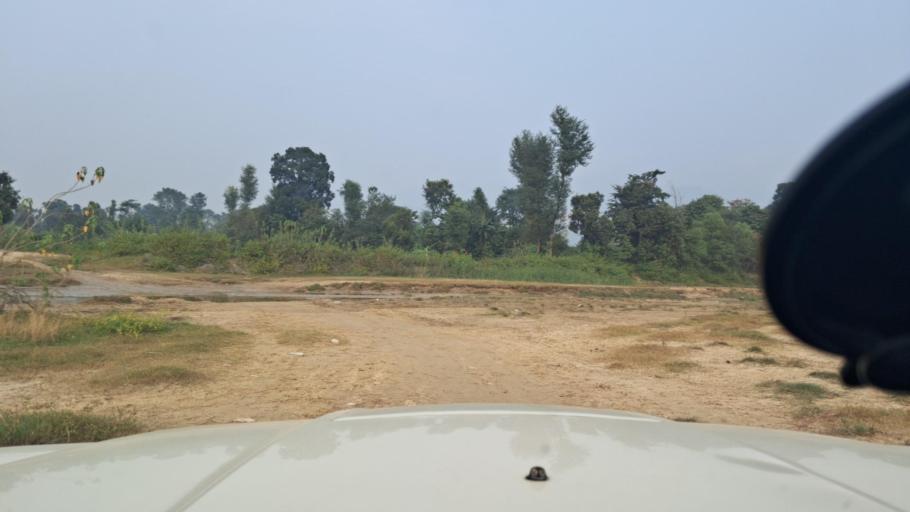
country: IN
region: Uttarakhand
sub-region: Udham Singh Nagar
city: Tanakpur
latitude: 29.0403
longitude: 80.1329
